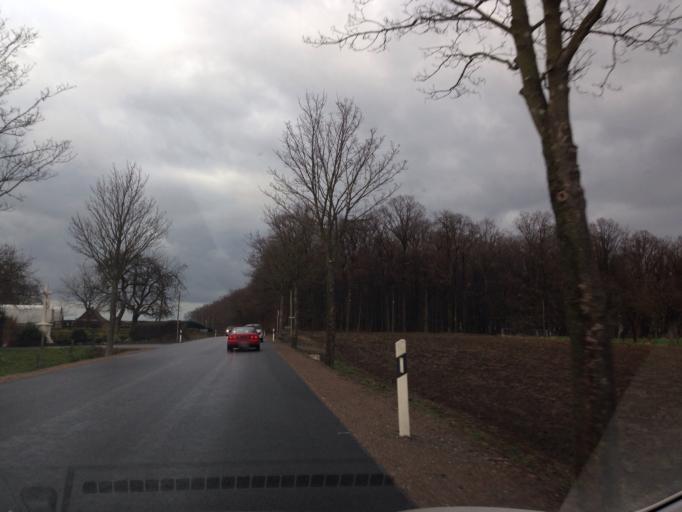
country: DE
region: North Rhine-Westphalia
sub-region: Regierungsbezirk Munster
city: Nordkirchen
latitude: 51.7737
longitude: 7.5453
